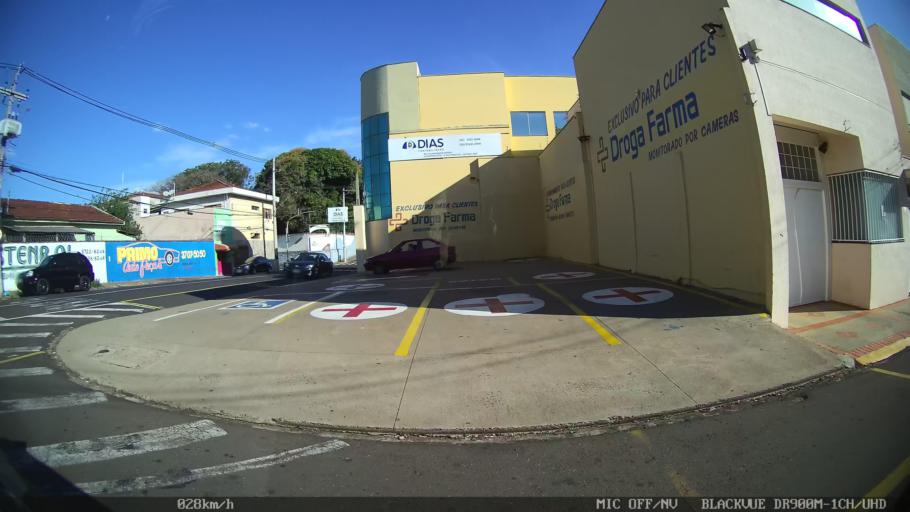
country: BR
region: Sao Paulo
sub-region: Franca
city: Franca
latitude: -20.5316
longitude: -47.4188
